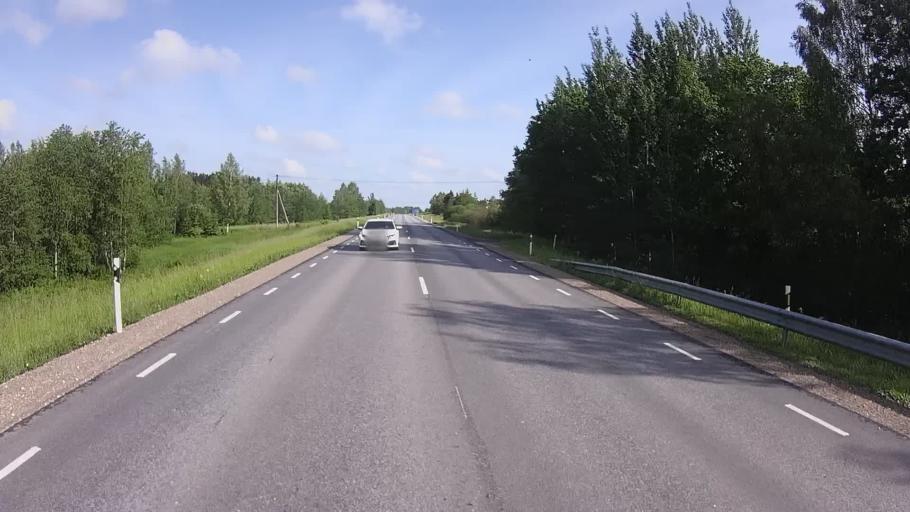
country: EE
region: Viljandimaa
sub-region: Viljandi linn
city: Viljandi
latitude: 58.3494
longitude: 25.5627
